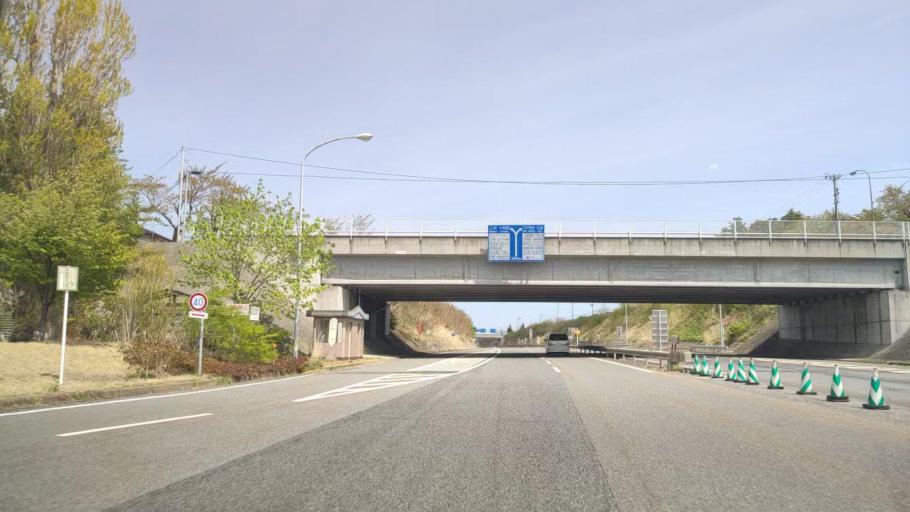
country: JP
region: Aomori
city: Hachinohe
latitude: 40.4870
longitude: 141.4630
